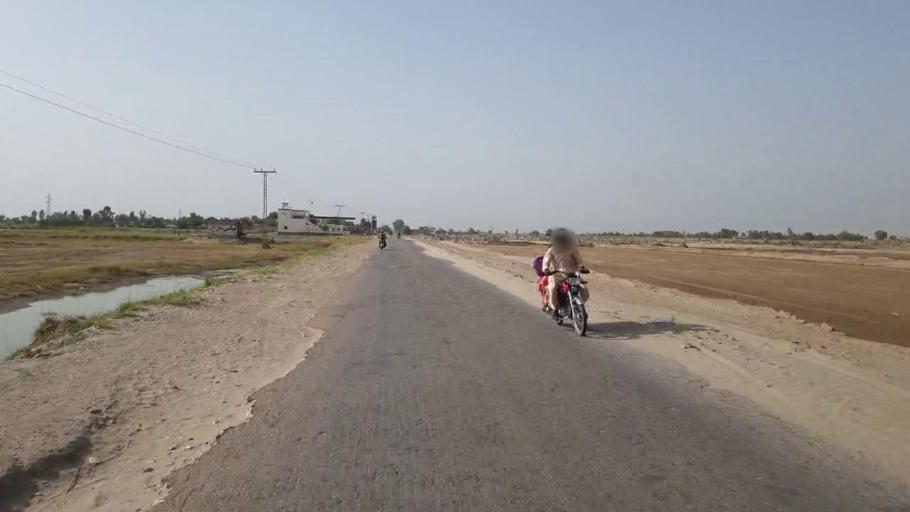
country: PK
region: Sindh
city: Sanghar
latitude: 26.2833
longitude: 68.9306
